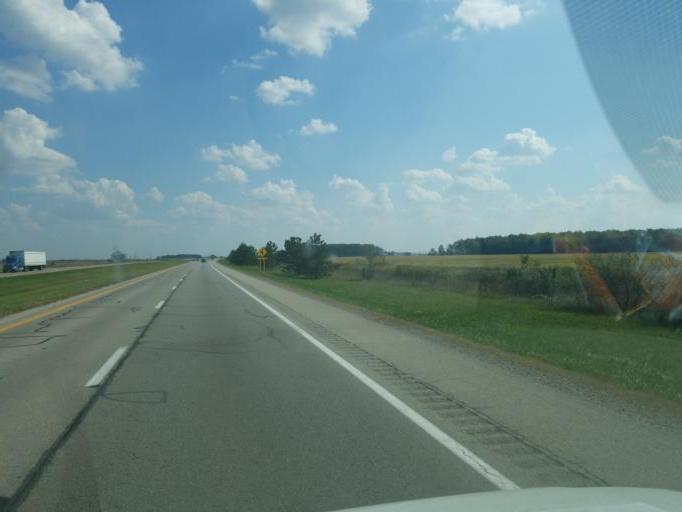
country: US
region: Indiana
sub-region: Allen County
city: Monroeville
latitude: 40.9861
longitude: -84.7784
